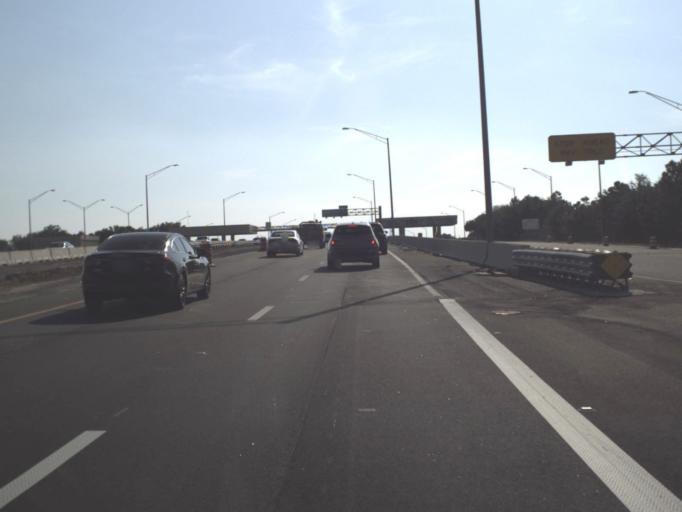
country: US
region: Florida
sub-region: Orange County
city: Orlovista
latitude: 28.5487
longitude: -81.4890
